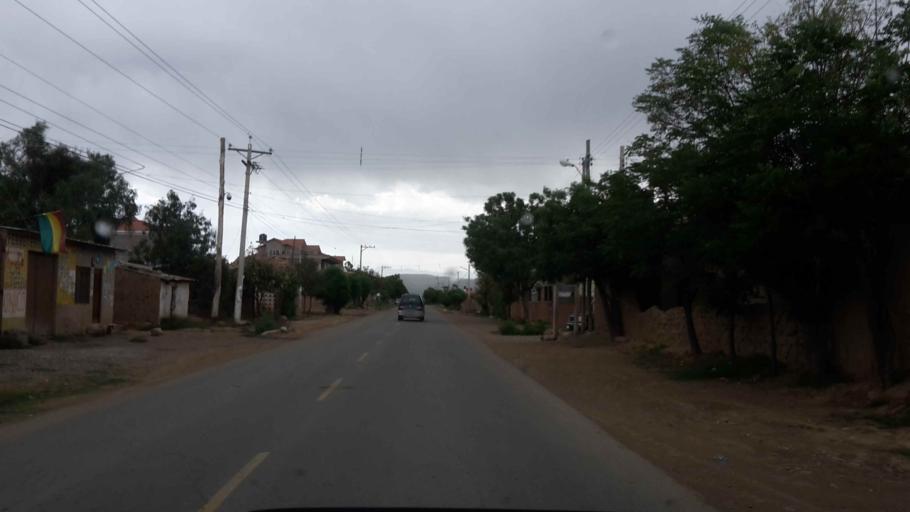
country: BO
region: Cochabamba
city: Tarata
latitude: -17.5844
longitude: -66.0523
